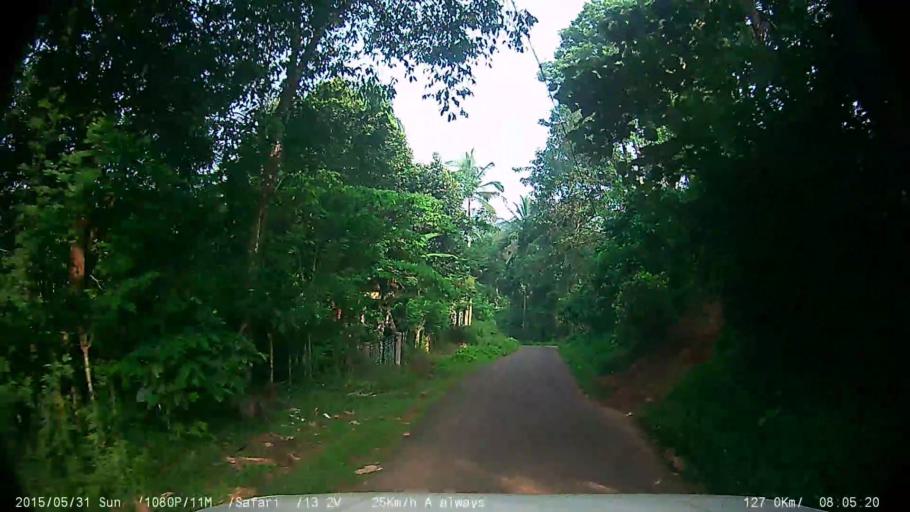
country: IN
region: Kerala
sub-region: Wayanad
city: Kalpetta
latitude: 11.6353
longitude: 76.0353
